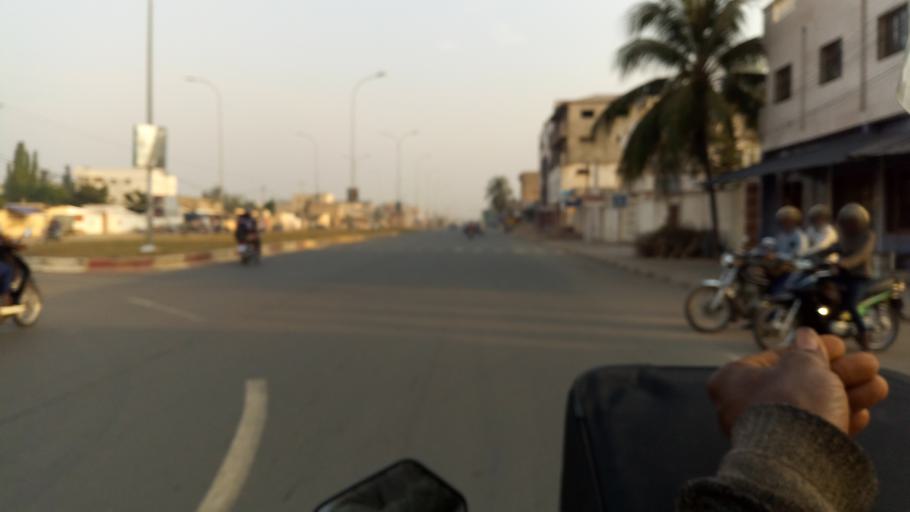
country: TG
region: Maritime
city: Lome
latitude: 6.2033
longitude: 1.1819
